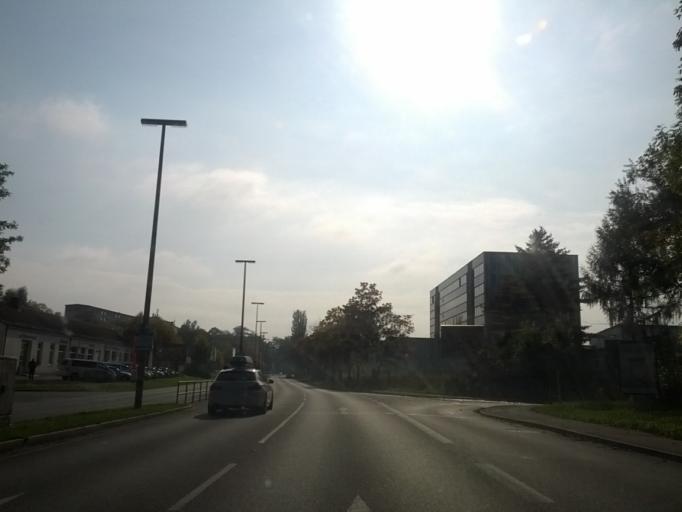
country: DE
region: Thuringia
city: Gera
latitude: 50.9030
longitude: 12.0691
